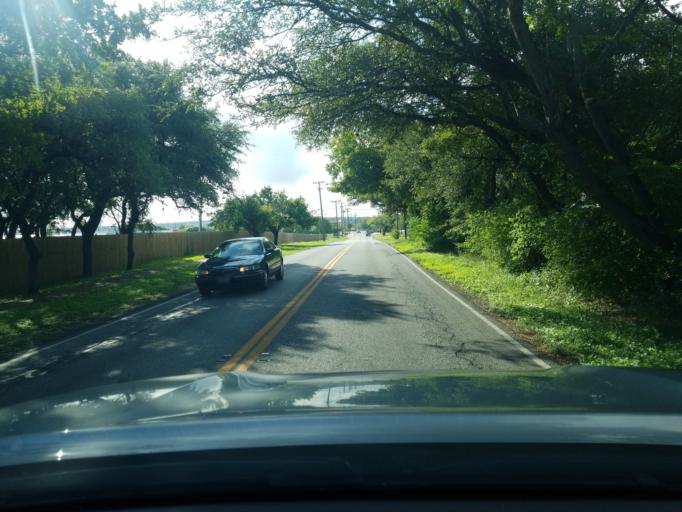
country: US
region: Texas
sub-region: Bexar County
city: Live Oak
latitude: 29.5919
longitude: -98.3577
